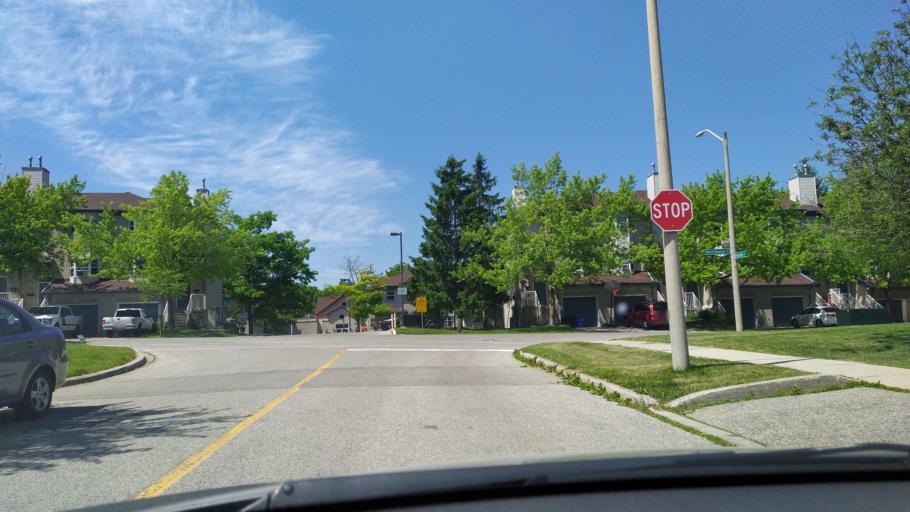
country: CA
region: Ontario
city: Waterloo
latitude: 43.4549
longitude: -80.5695
